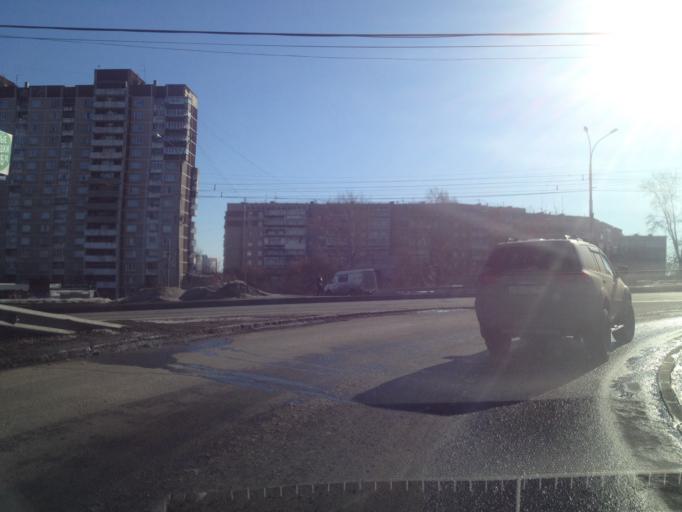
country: RU
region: Sverdlovsk
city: Yekaterinburg
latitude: 56.8424
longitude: 60.6722
